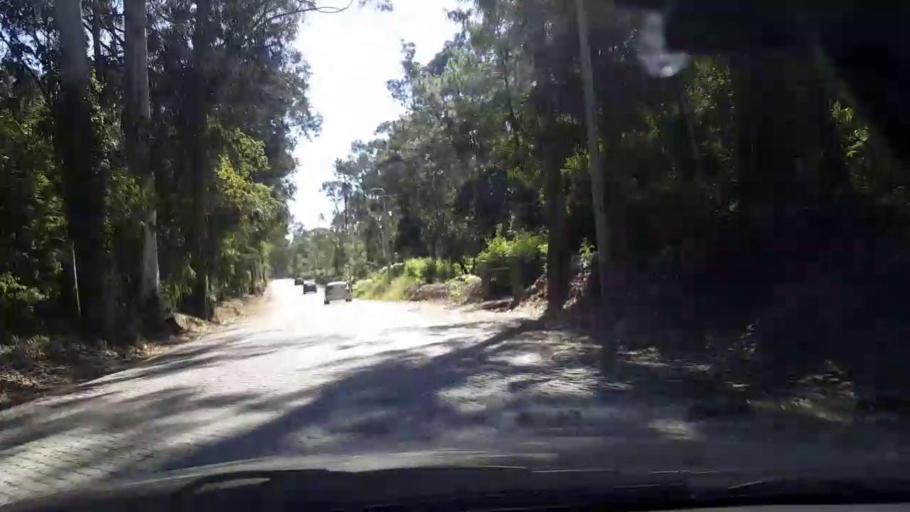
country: PT
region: Porto
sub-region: Vila do Conde
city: Arvore
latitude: 41.3266
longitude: -8.7271
